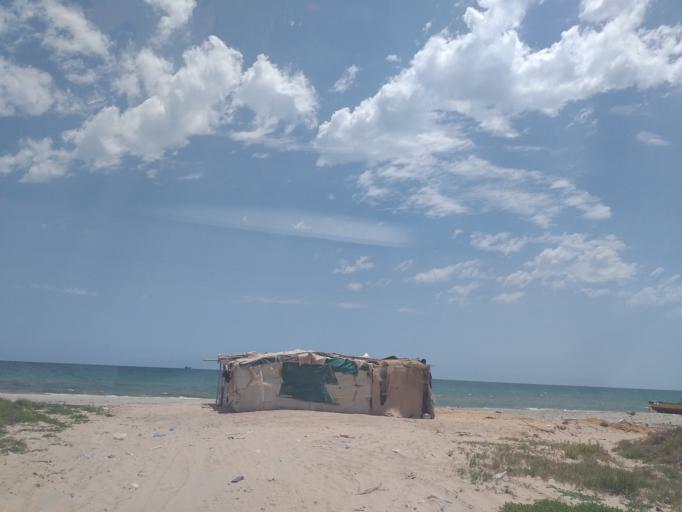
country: TN
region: Qabis
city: Gabes
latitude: 33.9472
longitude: 10.0752
